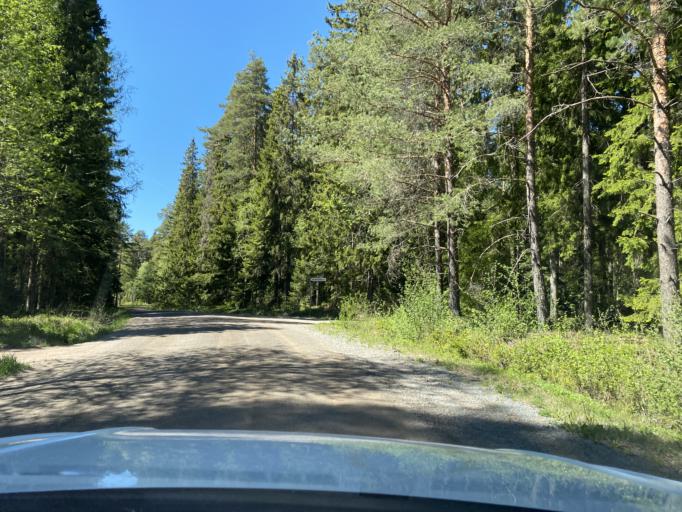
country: FI
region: Satakunta
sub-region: Rauma
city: Kiukainen
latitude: 61.1359
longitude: 21.9739
